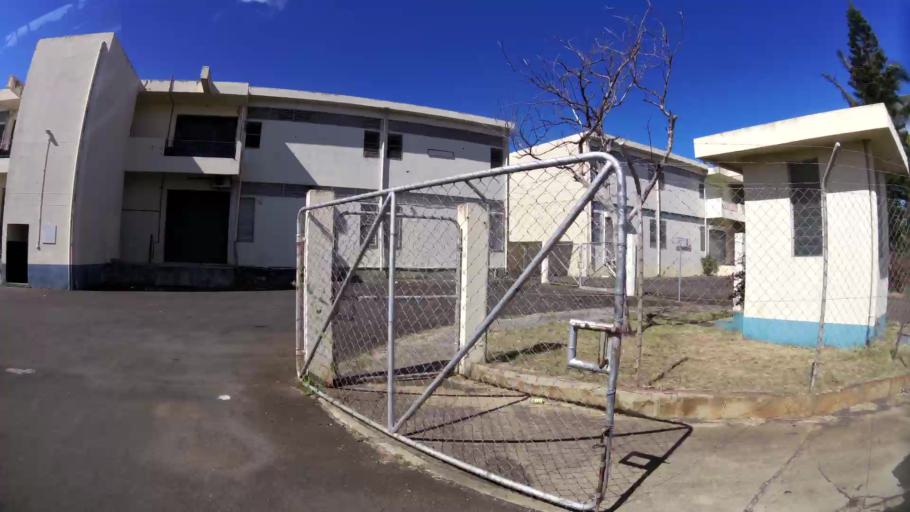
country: MU
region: Black River
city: Cascavelle
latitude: -20.2668
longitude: 57.4162
